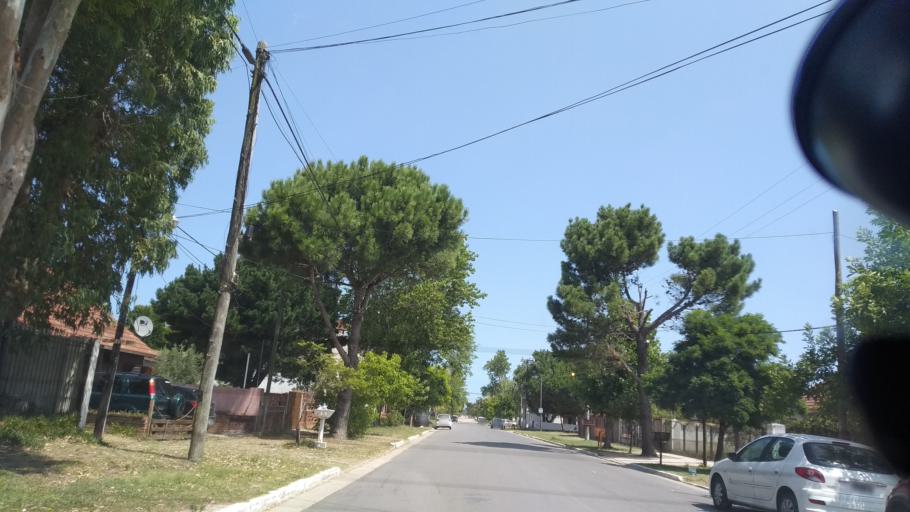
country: AR
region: Buenos Aires
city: Mar del Tuyu
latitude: -36.5795
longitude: -56.6936
